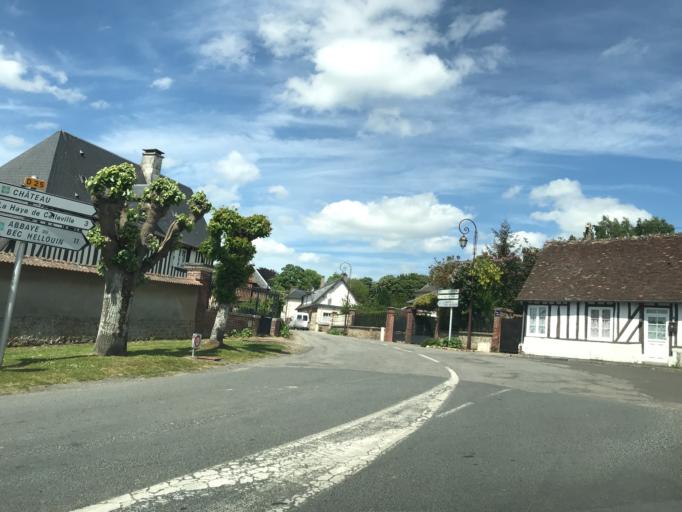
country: FR
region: Haute-Normandie
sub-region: Departement de l'Eure
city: Nassandres
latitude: 49.1671
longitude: 0.7847
